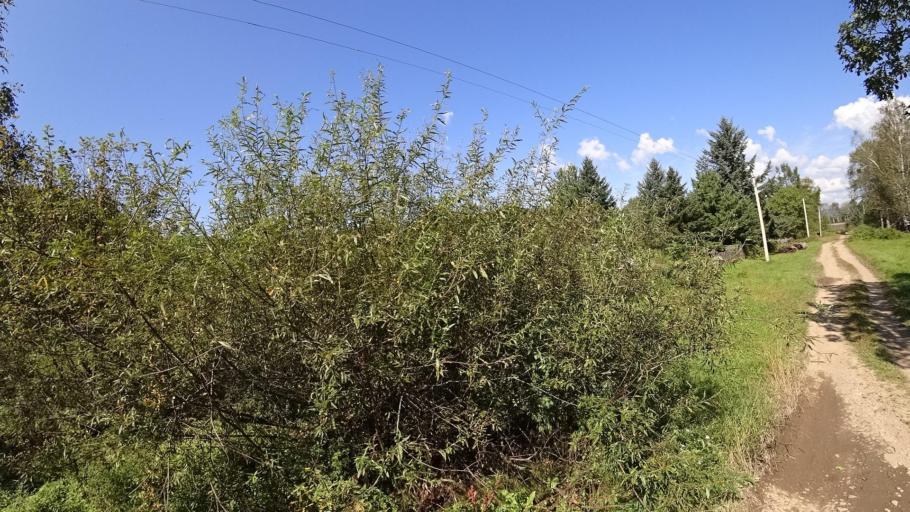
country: RU
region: Jewish Autonomous Oblast
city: Londoko
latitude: 49.0127
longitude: 132.2297
